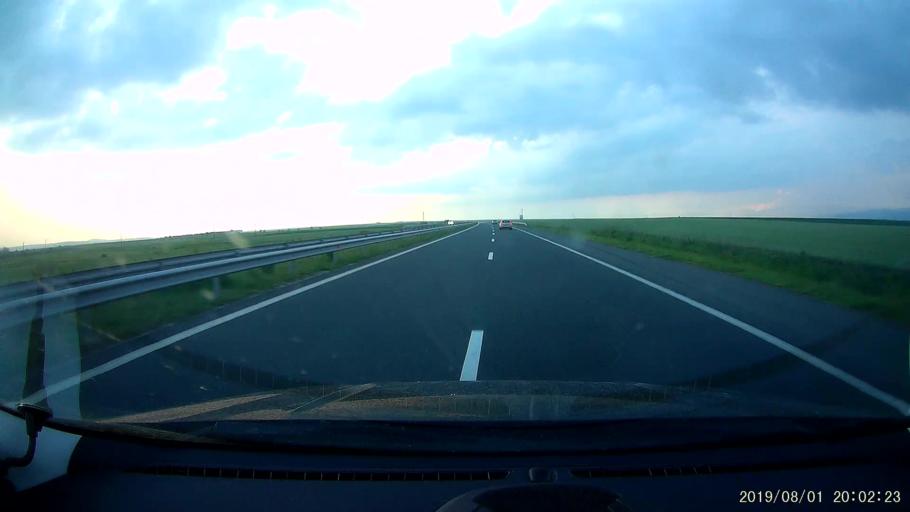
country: BG
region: Yambol
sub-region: Obshtina Straldzha
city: Straldzha
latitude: 42.5595
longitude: 26.6314
